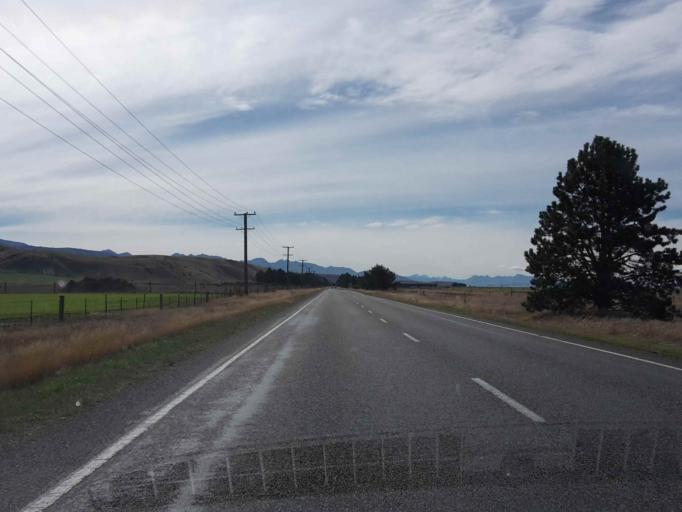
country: NZ
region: Otago
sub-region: Queenstown-Lakes District
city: Wanaka
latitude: -44.3947
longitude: 169.9951
